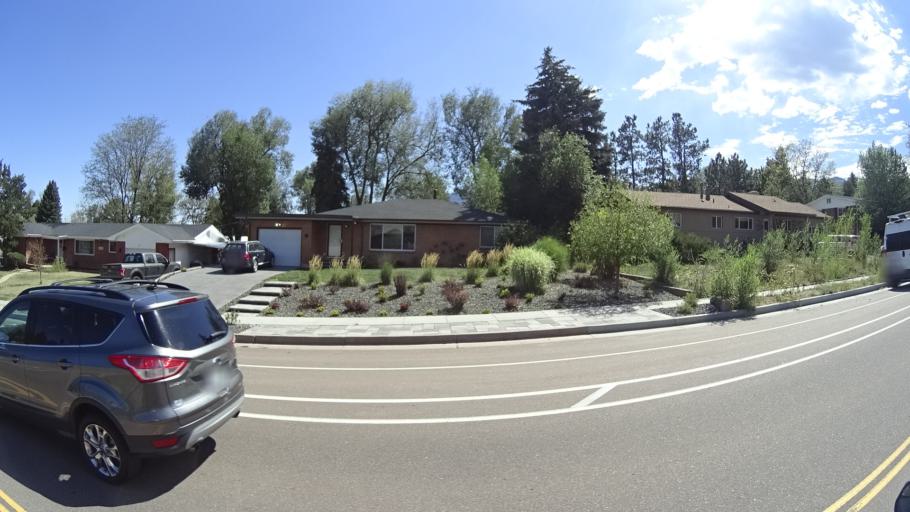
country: US
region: Colorado
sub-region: El Paso County
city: Colorado Springs
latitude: 38.8124
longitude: -104.8488
